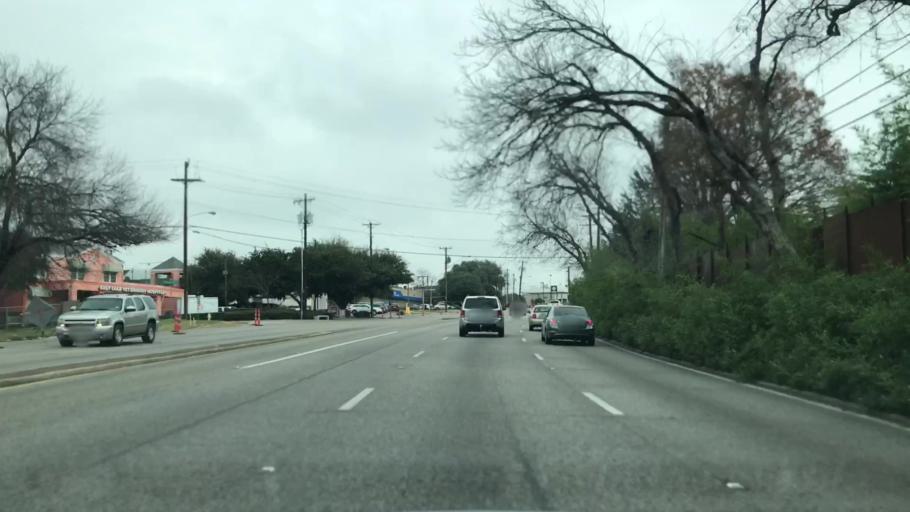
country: US
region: Texas
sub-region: Dallas County
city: Highland Park
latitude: 32.8638
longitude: -96.7134
